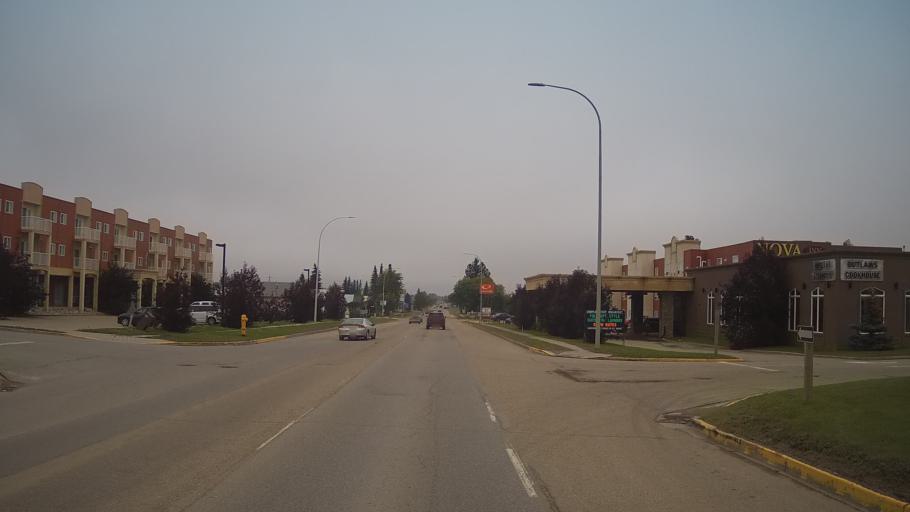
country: CA
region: Alberta
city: Edson
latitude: 53.5762
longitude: -116.4477
